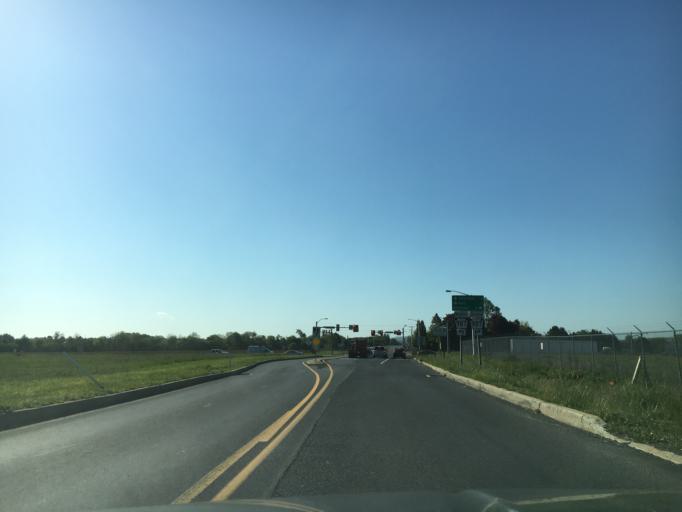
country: US
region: Pennsylvania
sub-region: Lehigh County
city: Catasauqua
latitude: 40.6630
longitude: -75.4243
